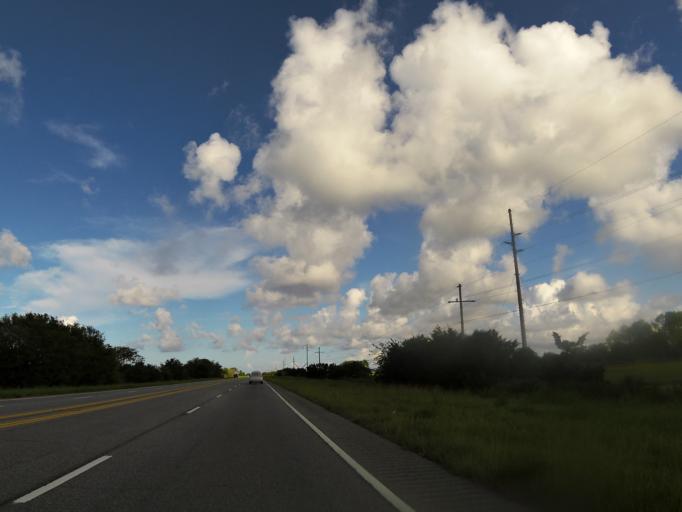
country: US
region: Georgia
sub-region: Glynn County
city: Brunswick
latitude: 31.1103
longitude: -81.5189
